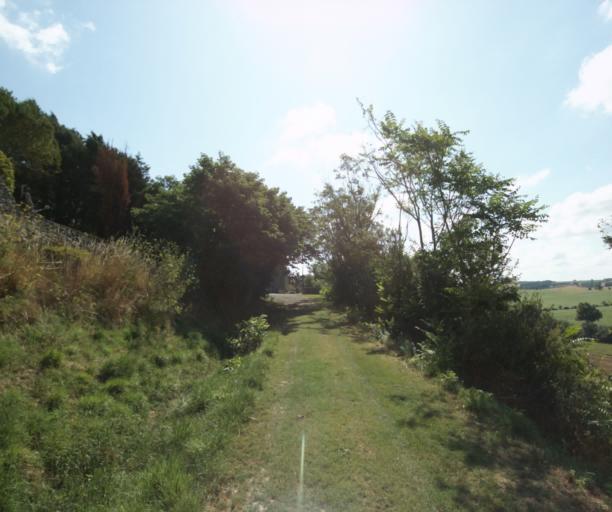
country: FR
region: Midi-Pyrenees
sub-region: Departement de la Haute-Garonne
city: Avignonet-Lauragais
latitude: 43.4489
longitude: 1.7887
